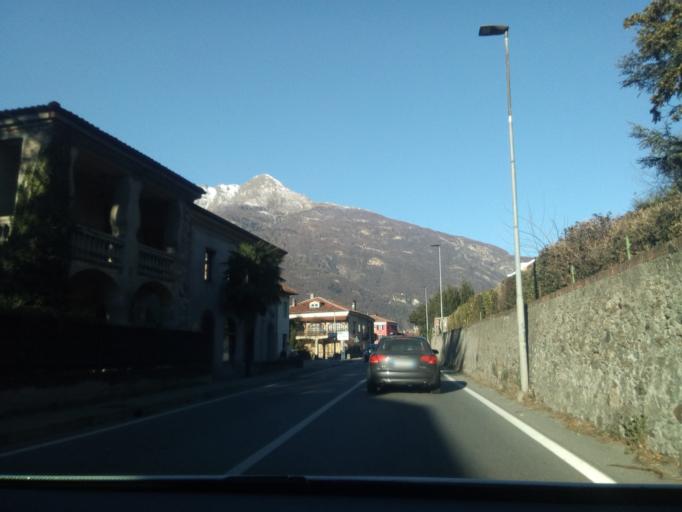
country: IT
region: Piedmont
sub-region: Provincia di Torino
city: Settimo Vittone
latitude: 45.5471
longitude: 7.8323
